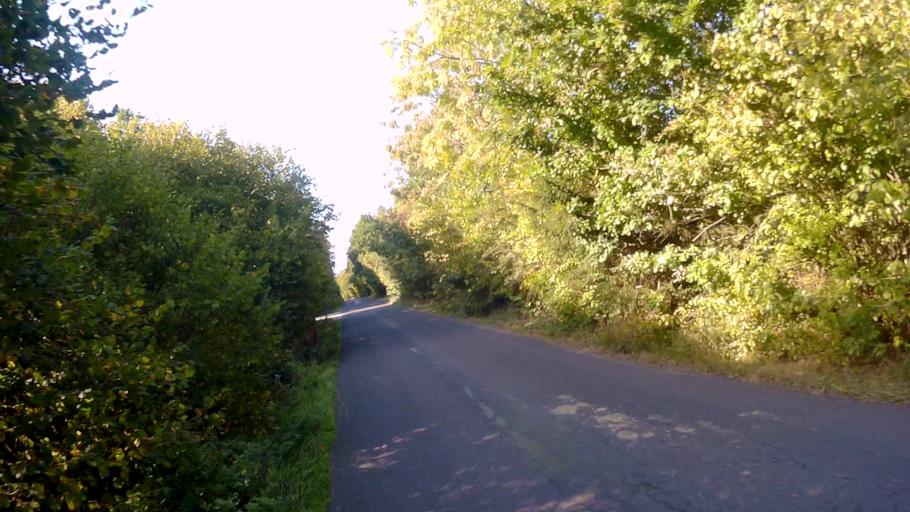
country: GB
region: England
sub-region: Hampshire
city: Lindford
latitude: 51.1631
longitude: -0.8404
